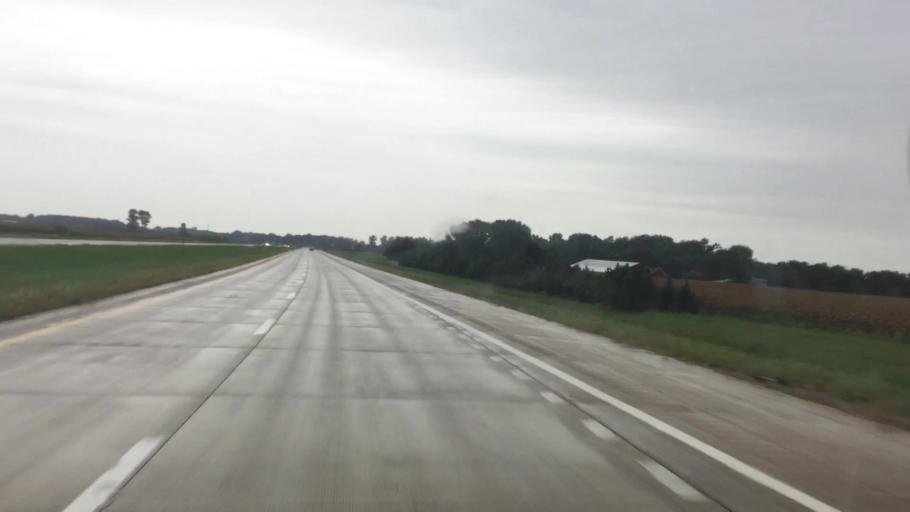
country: US
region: Ohio
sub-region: Lucas County
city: Whitehouse
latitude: 41.4558
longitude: -83.8308
